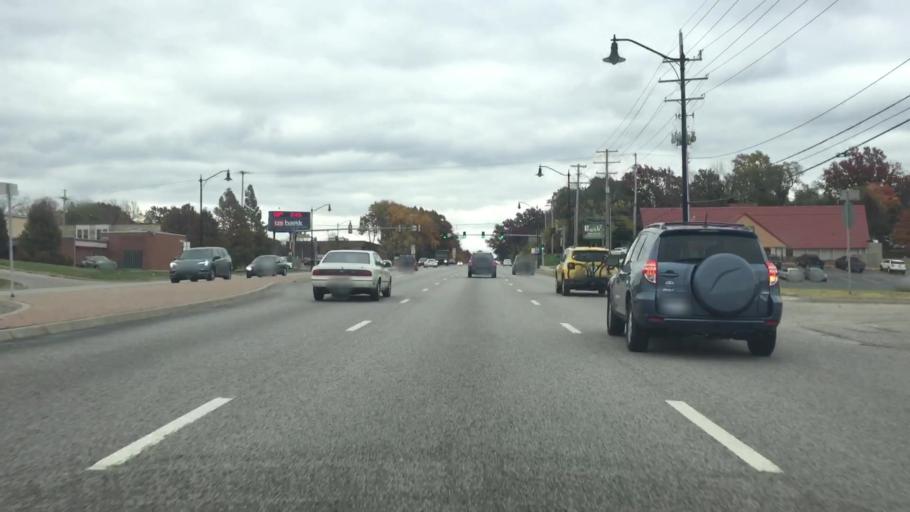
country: US
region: Kansas
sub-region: Johnson County
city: Merriam
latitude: 39.0148
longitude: -94.6882
